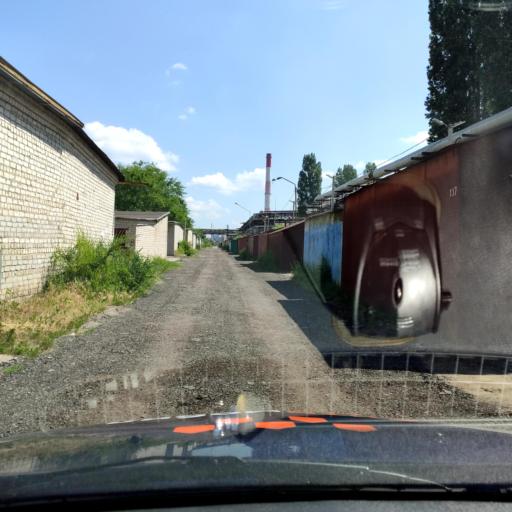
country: RU
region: Voronezj
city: Voronezh
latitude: 51.6305
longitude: 39.2423
